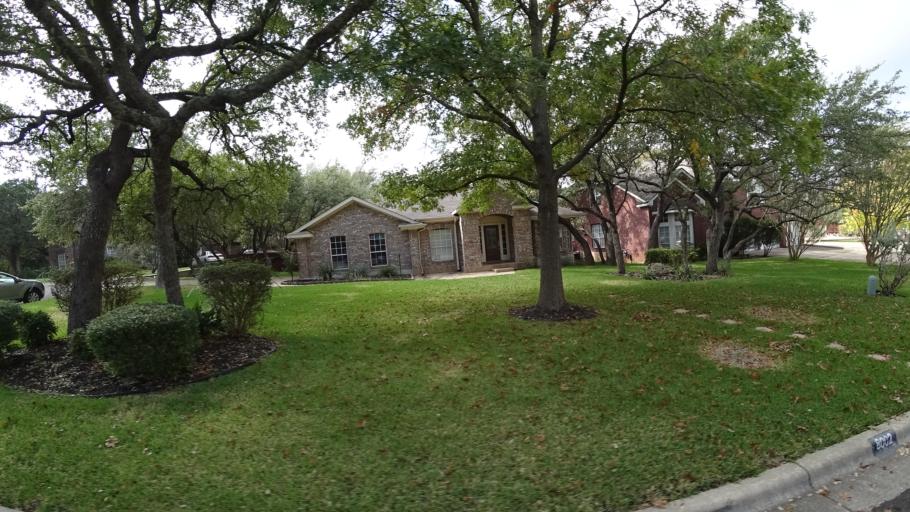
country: US
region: Texas
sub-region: Williamson County
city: Anderson Mill
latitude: 30.4192
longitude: -97.8571
